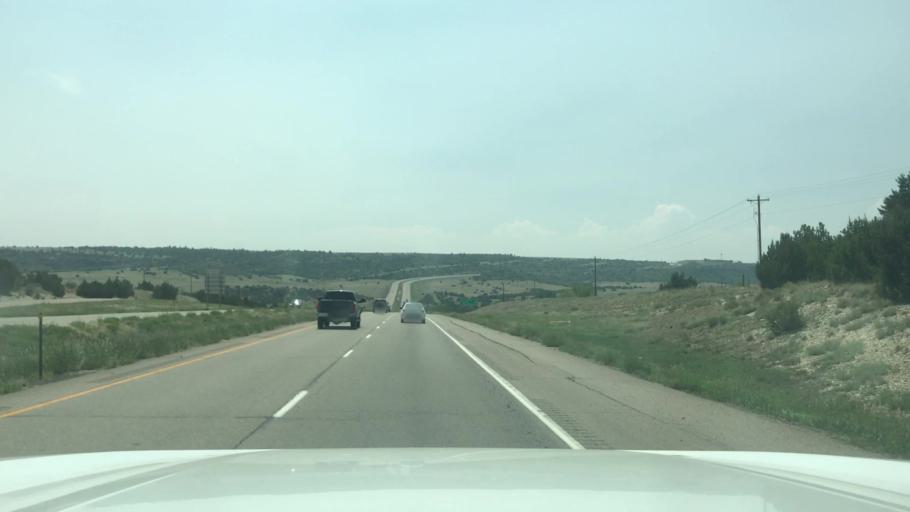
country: US
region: Colorado
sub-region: Pueblo County
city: Colorado City
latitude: 37.9555
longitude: -104.8007
